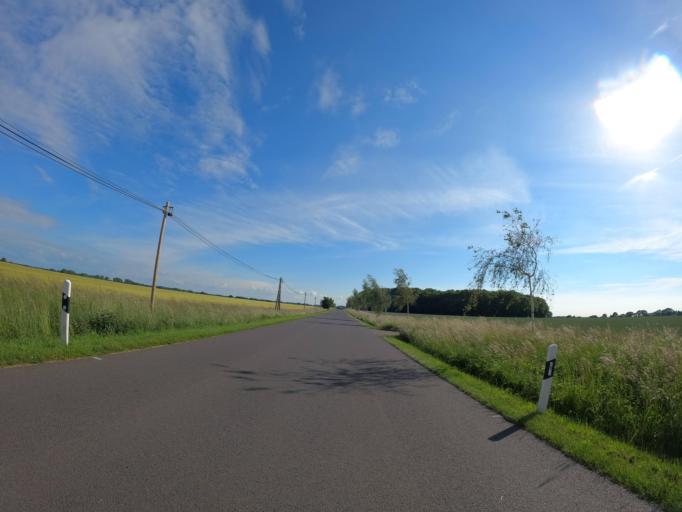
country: DE
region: Mecklenburg-Vorpommern
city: Preetz
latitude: 54.3485
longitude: 12.9880
